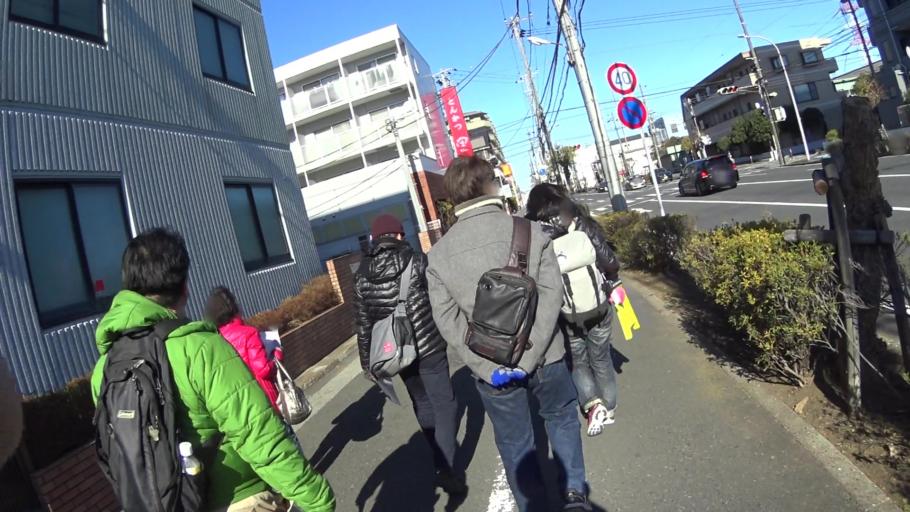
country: JP
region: Tokyo
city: Urayasu
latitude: 35.6464
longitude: 139.8882
